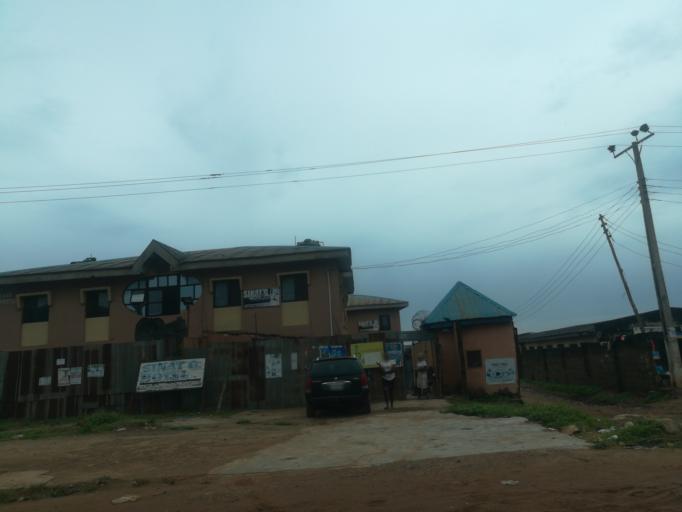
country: NG
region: Oyo
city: Ibadan
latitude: 7.3918
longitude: 3.9607
